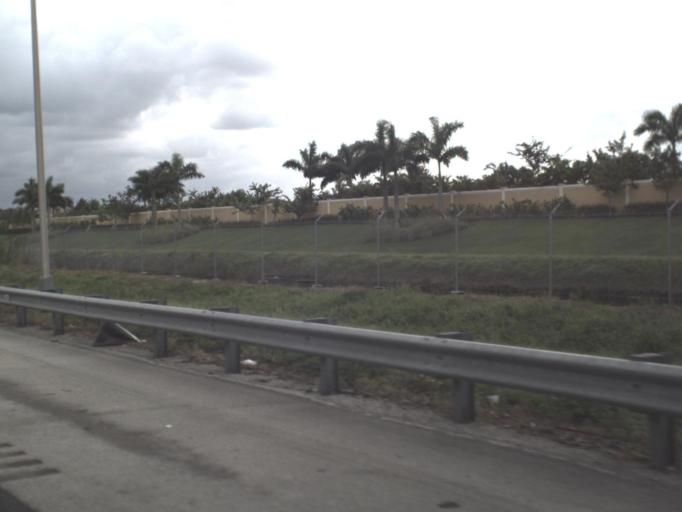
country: US
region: Florida
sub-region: Palm Beach County
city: Villages of Oriole
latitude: 26.5096
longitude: -80.1727
